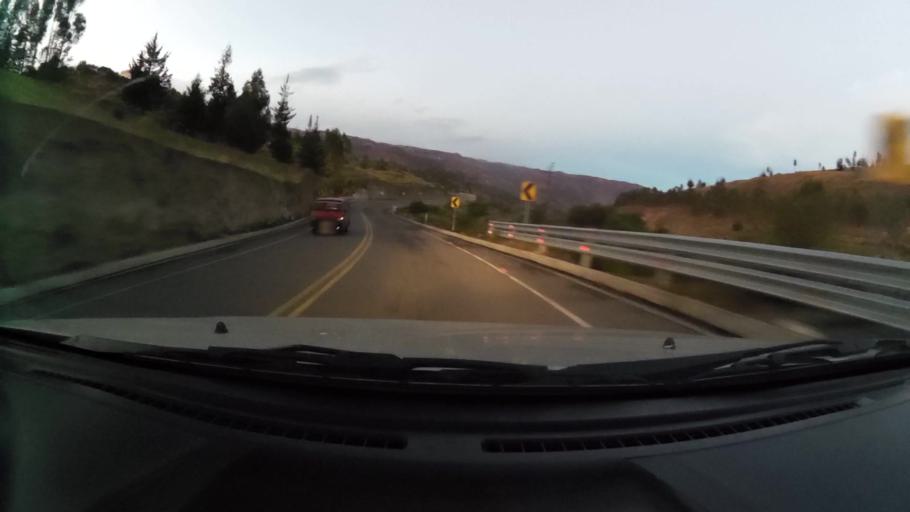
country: EC
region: Chimborazo
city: Riobamba
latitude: -1.9003
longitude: -78.6913
